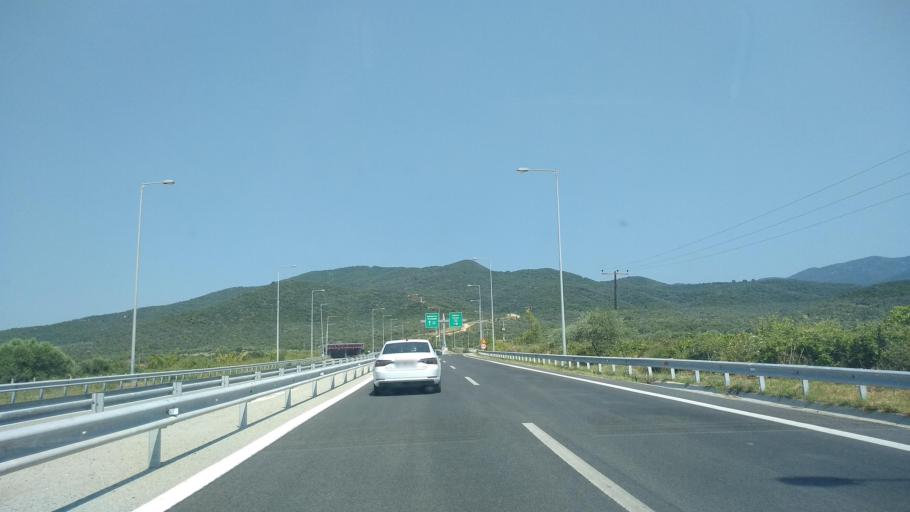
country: GR
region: Central Macedonia
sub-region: Nomos Thessalonikis
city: Nea Vrasna
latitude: 40.7081
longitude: 23.6855
